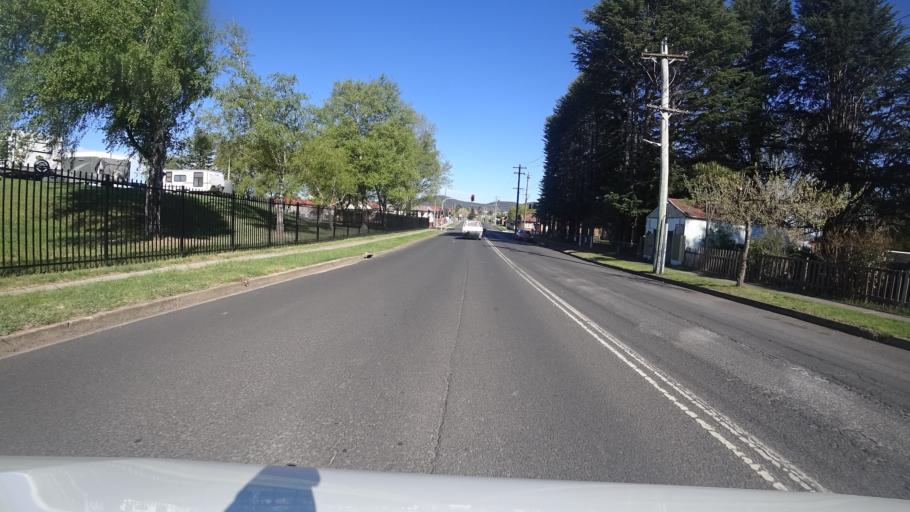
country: AU
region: New South Wales
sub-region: Lithgow
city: Lithgow
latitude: -33.4872
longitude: 150.1409
